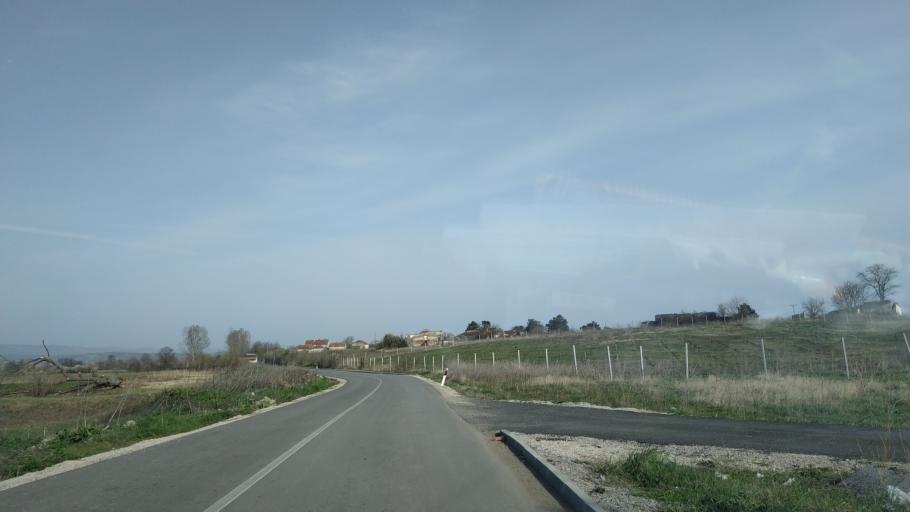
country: RS
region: Central Serbia
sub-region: Nisavski Okrug
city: Aleksinac
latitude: 43.5163
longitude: 21.6733
